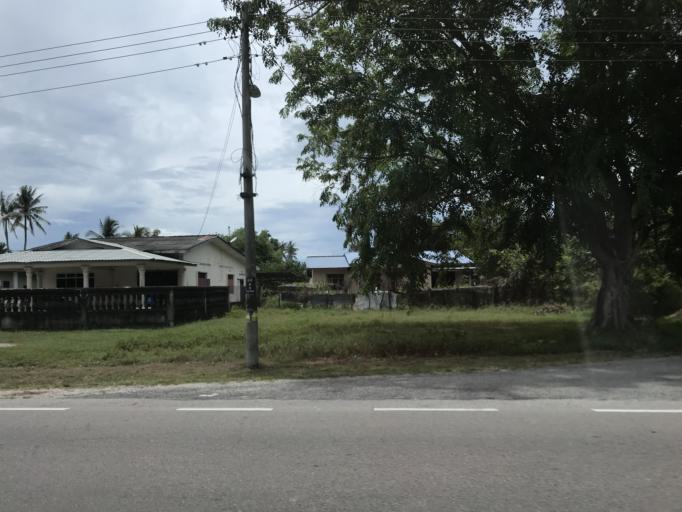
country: MY
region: Kelantan
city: Tumpat
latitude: 6.1758
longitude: 102.1972
